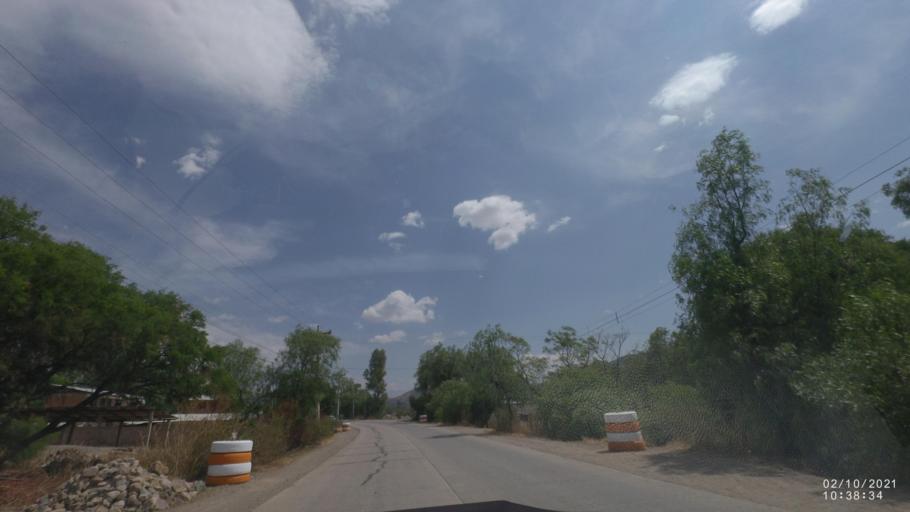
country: BO
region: Cochabamba
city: Capinota
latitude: -17.6333
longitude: -66.2655
